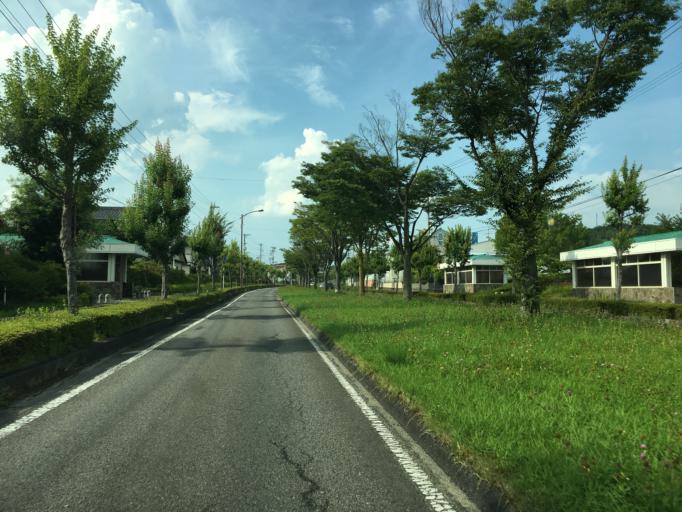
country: JP
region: Fukushima
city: Koriyama
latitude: 37.3815
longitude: 140.4350
